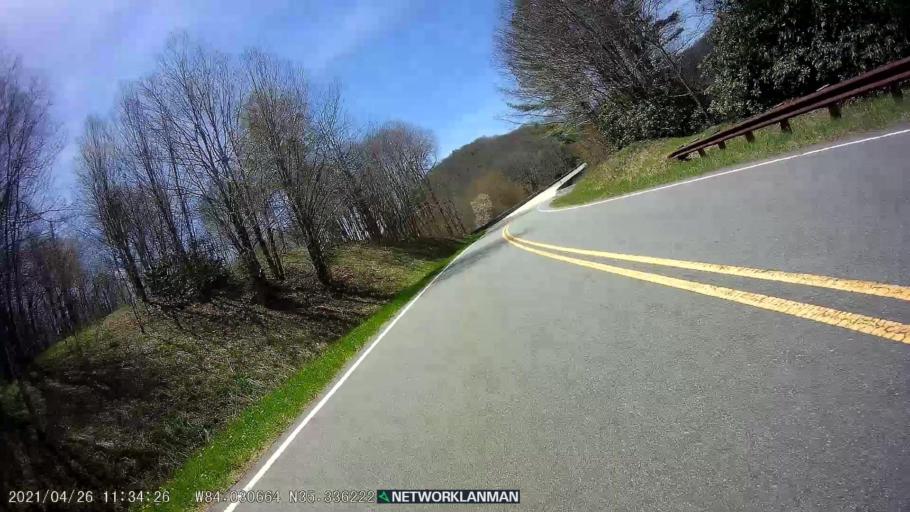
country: US
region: North Carolina
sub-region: Graham County
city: Robbinsville
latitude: 35.3361
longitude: -84.0303
